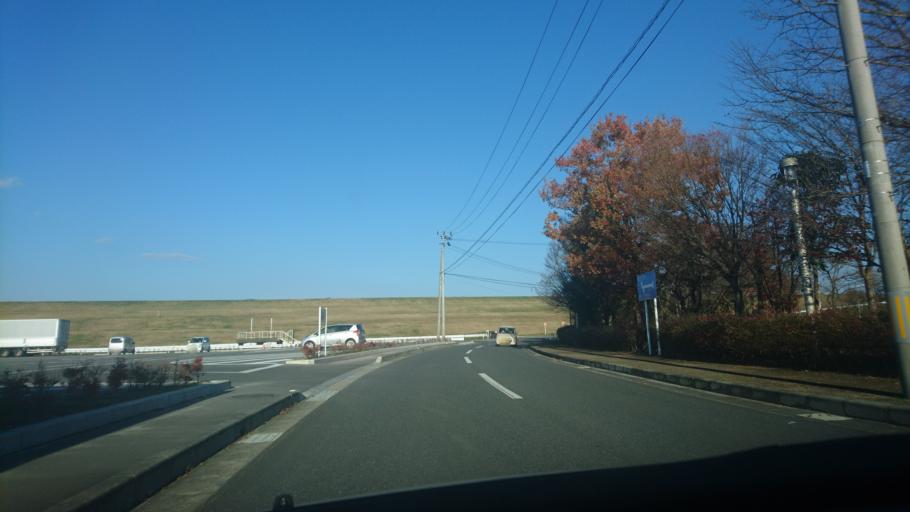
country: JP
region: Iwate
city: Ichinoseki
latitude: 38.9414
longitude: 141.1551
